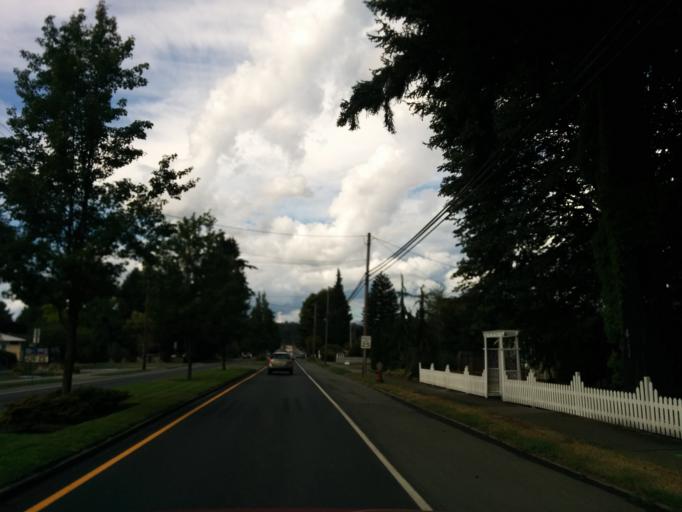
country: US
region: Washington
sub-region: Snohomish County
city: Monroe
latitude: 47.8516
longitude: -121.9707
